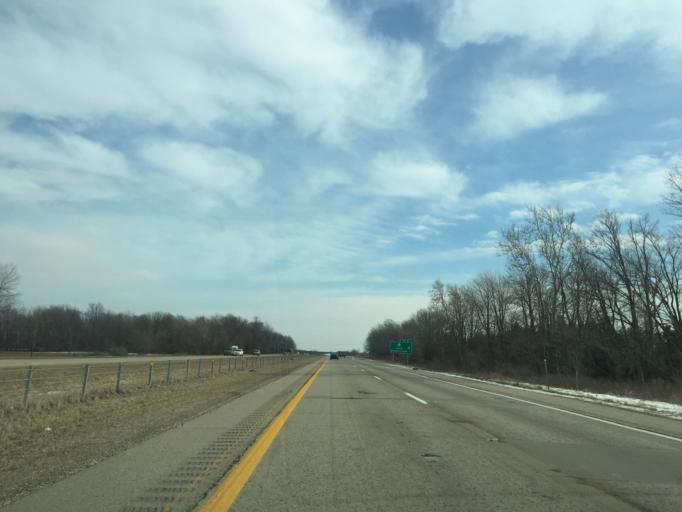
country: US
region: Michigan
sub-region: Ionia County
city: Lake Odessa
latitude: 42.8791
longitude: -85.0864
